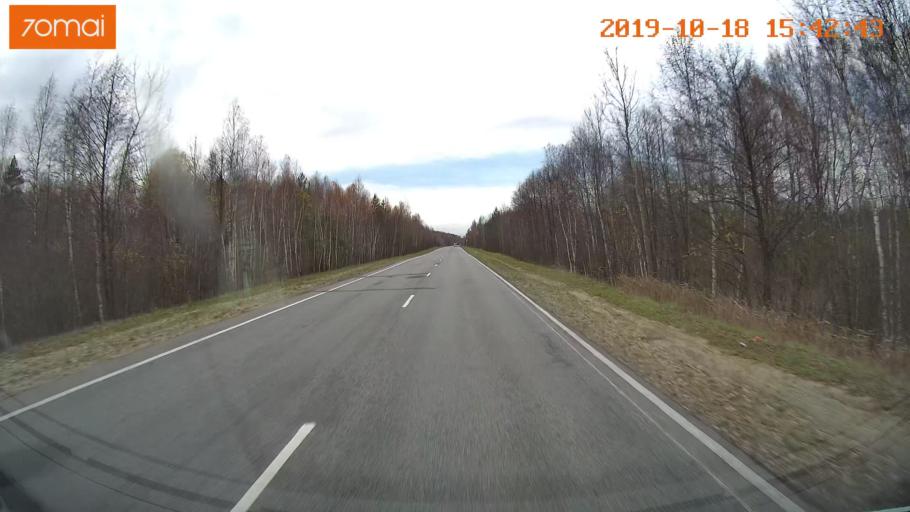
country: RU
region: Vladimir
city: Golovino
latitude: 55.9583
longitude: 40.5635
